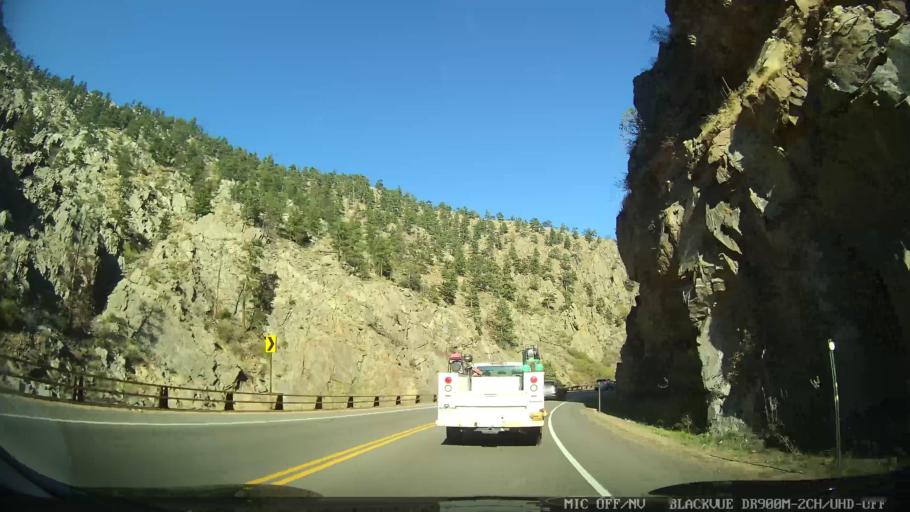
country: US
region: Colorado
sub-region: Larimer County
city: Loveland
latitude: 40.4244
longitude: -105.2385
